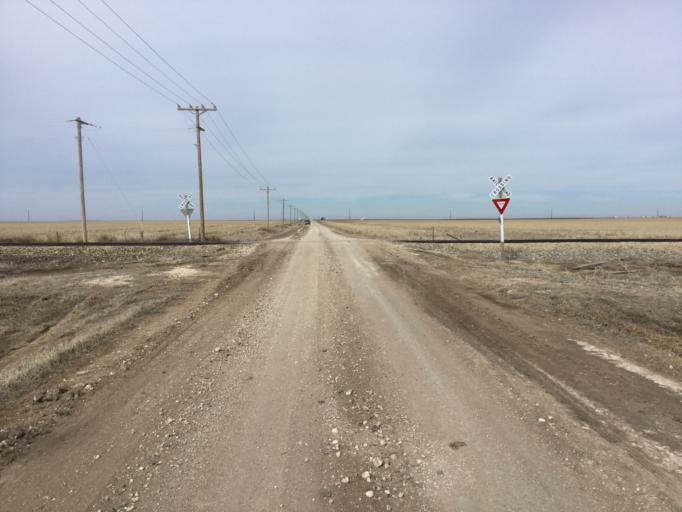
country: US
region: Kansas
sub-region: Lane County
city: Dighton
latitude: 38.4836
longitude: -100.6498
